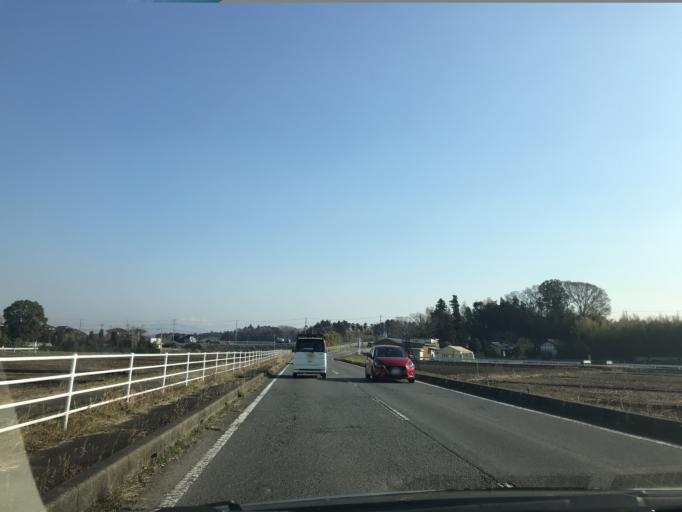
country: JP
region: Ibaraki
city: Mitsukaido
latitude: 36.0672
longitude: 140.0126
